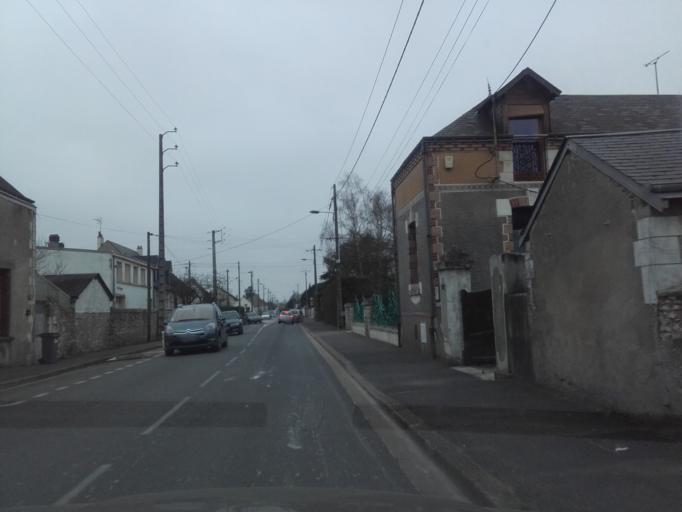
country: FR
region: Centre
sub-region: Departement d'Indre-et-Loire
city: Saint-Cyr-sur-Loire
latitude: 47.3852
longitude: 0.6431
